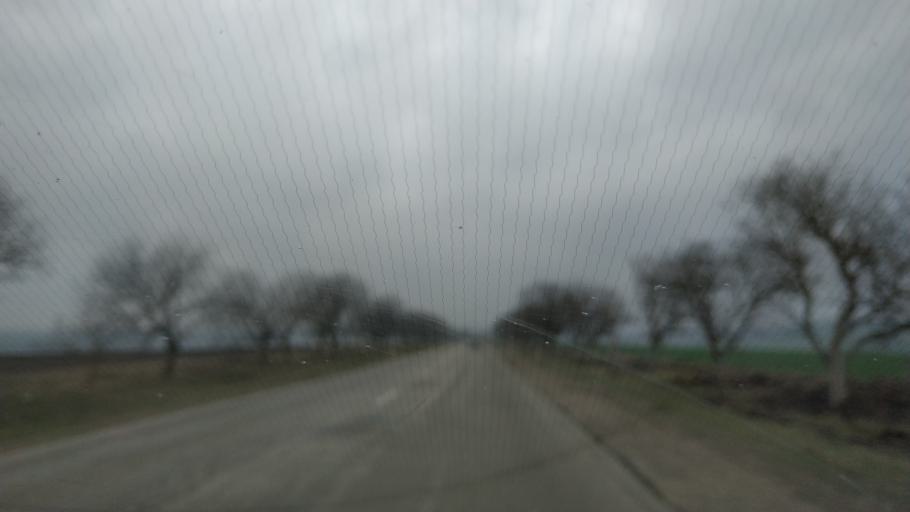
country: MD
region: Gagauzia
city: Comrat
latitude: 46.2590
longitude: 28.7509
